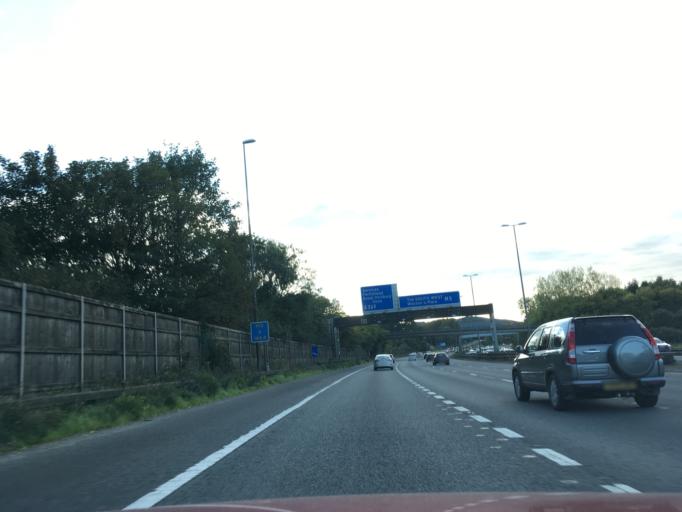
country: GB
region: England
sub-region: North Somerset
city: Easton-in-Gordano
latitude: 51.4808
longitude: -2.7022
